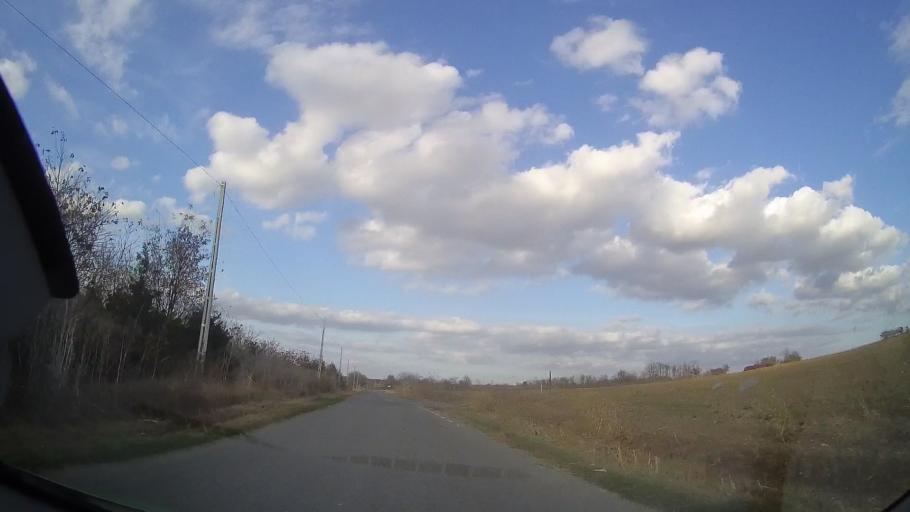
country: RO
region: Constanta
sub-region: Comuna Cerchezu
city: Cerchezu
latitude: 43.8510
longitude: 28.1005
